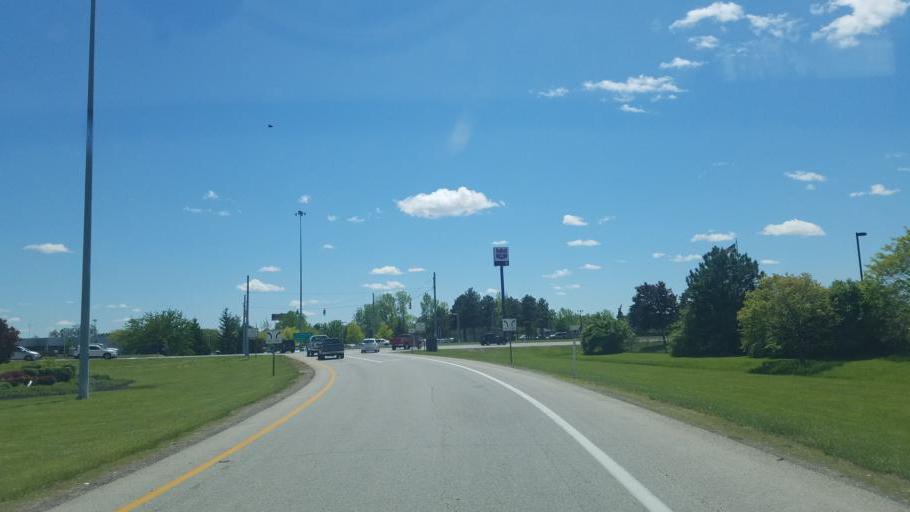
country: US
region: Ohio
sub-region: Franklin County
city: Hilliard
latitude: 40.0338
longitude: -83.1264
